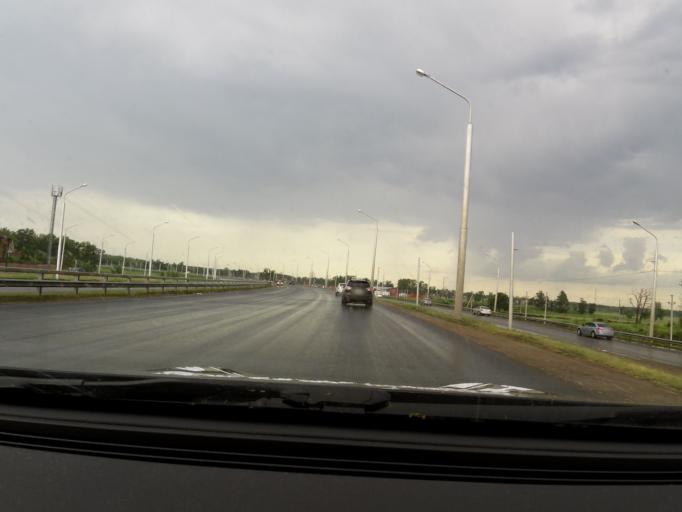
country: RU
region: Bashkortostan
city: Ufa
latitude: 54.7724
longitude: 55.9538
